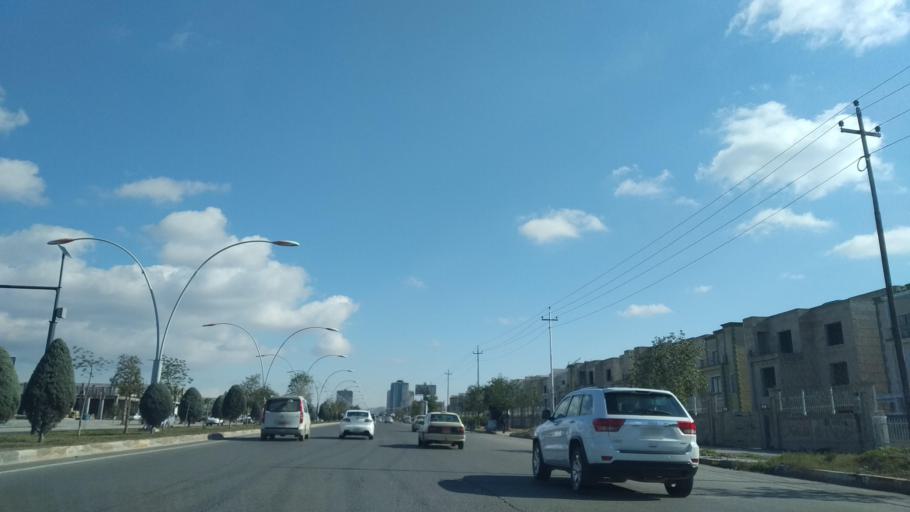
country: IQ
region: Arbil
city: Erbil
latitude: 36.2024
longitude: 44.1046
